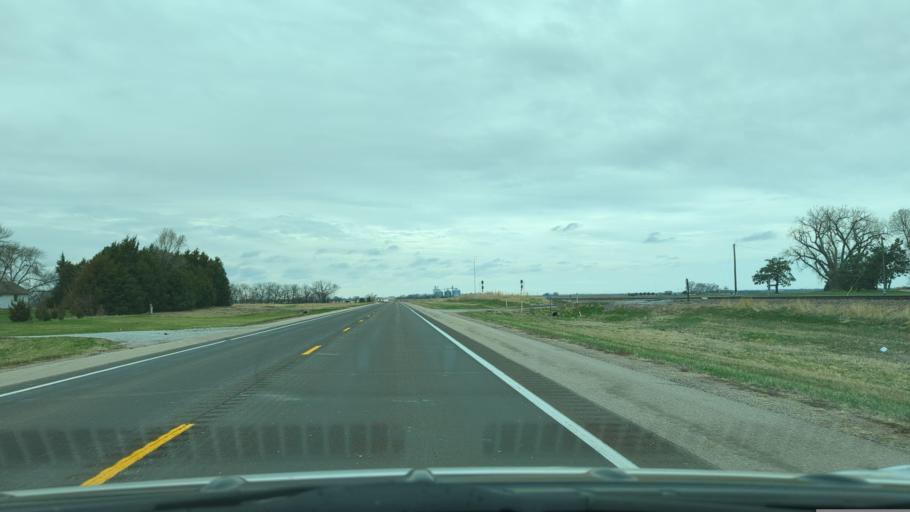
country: US
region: Nebraska
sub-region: Lancaster County
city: Waverly
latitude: 40.9374
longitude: -96.4871
